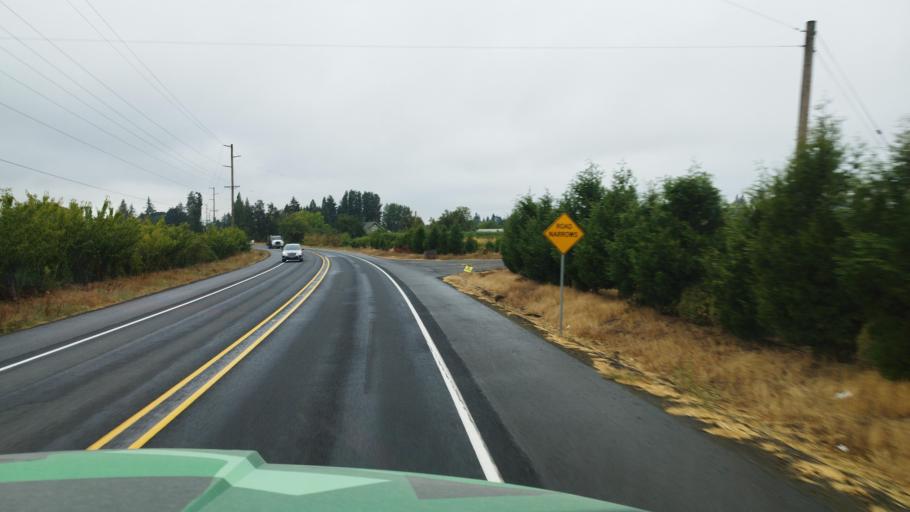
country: US
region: Oregon
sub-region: Washington County
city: Cornelius
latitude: 45.5362
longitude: -123.0783
